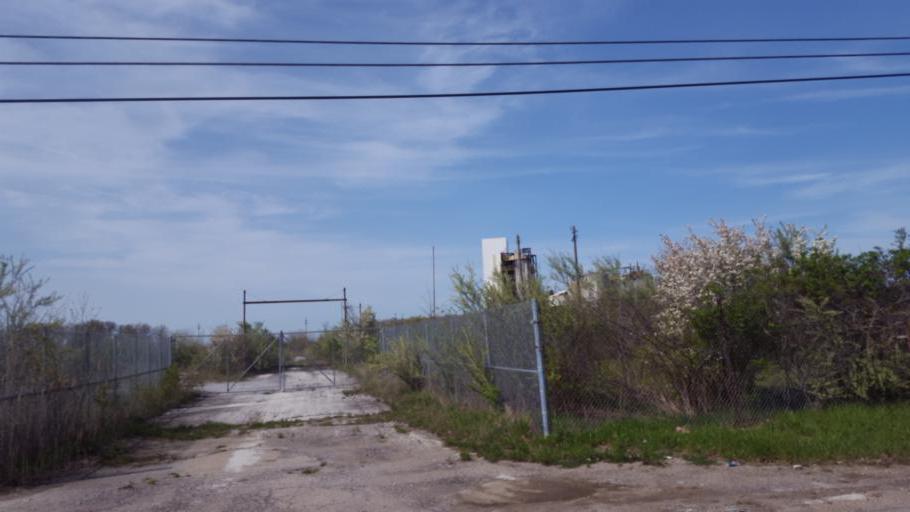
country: US
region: Ohio
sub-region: Lake County
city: Painesville
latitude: 41.7547
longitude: -81.2348
